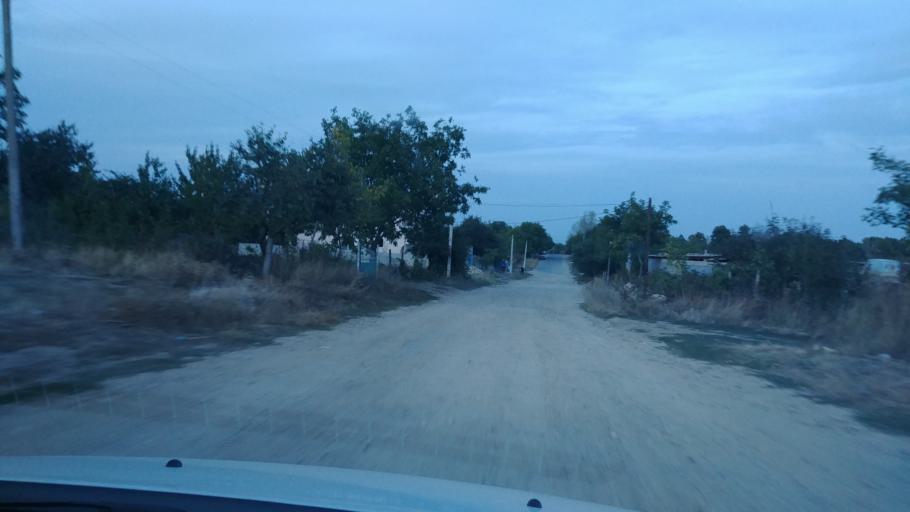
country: MD
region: Rezina
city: Saharna
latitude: 47.6718
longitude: 28.9517
